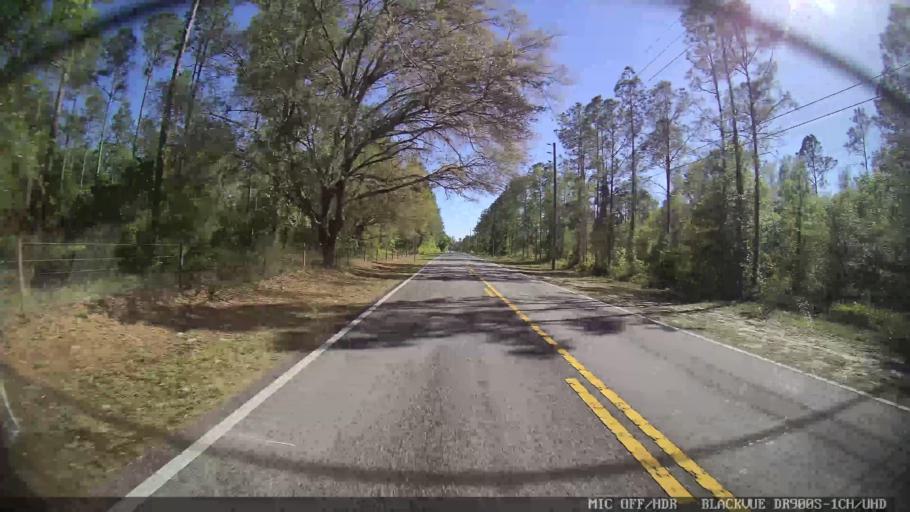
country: US
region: Florida
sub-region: Pasco County
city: Shady Hills
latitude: 28.3560
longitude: -82.5425
